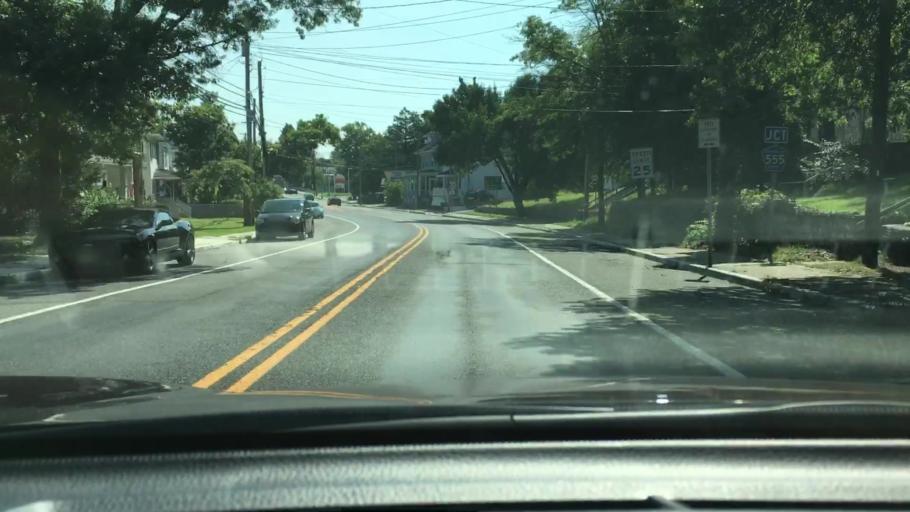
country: US
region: New Jersey
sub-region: Cumberland County
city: Millville
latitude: 39.3955
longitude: -75.0439
